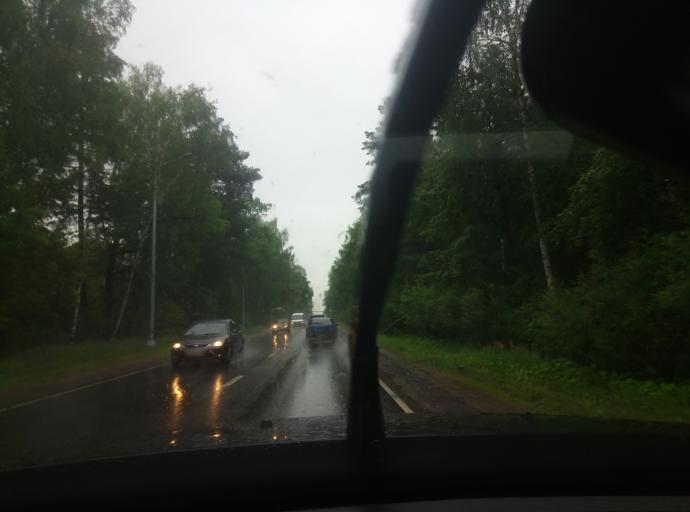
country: RU
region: Moskovskaya
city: Protvino
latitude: 54.8859
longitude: 37.1879
